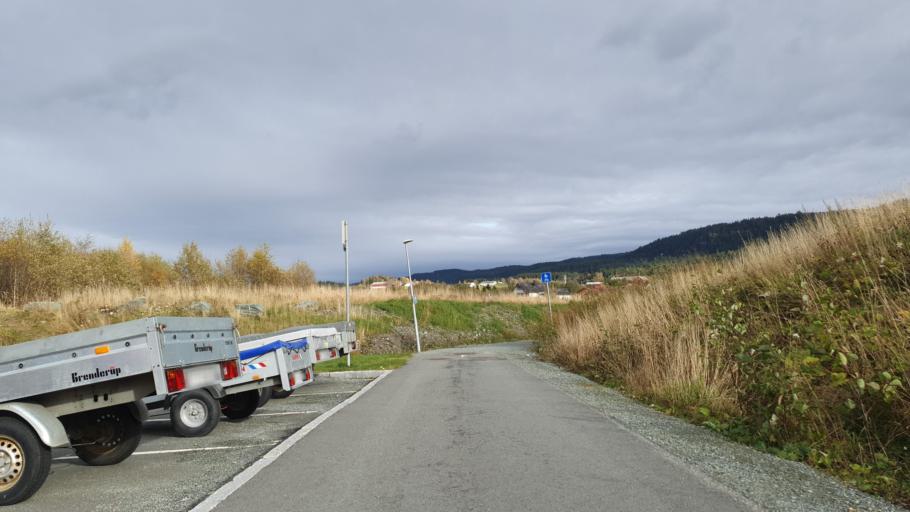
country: NO
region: Sor-Trondelag
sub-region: Klaebu
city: Klaebu
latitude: 63.3046
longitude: 10.4690
